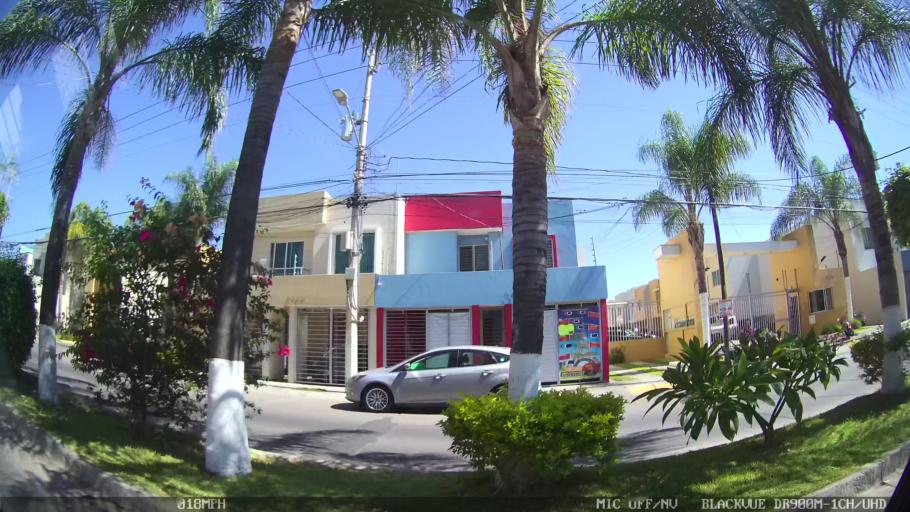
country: MX
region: Jalisco
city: Tlaquepaque
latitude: 20.6469
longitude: -103.2845
